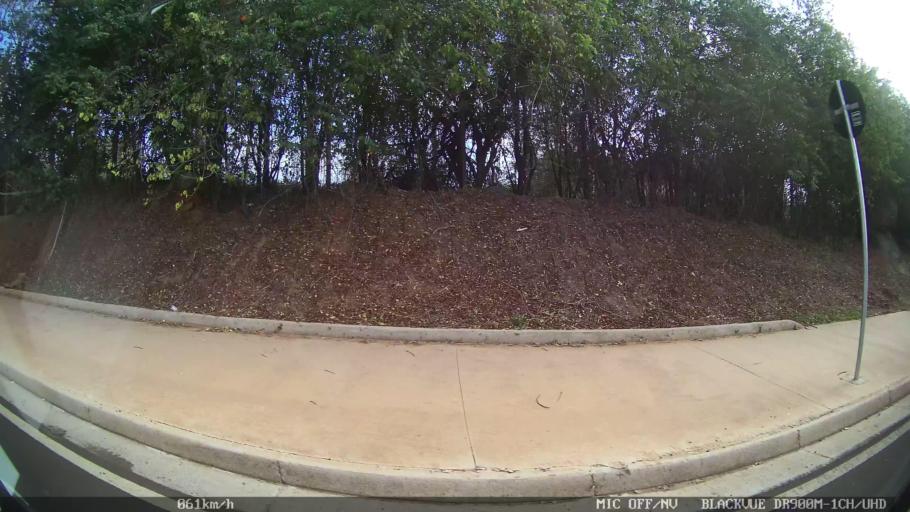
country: BR
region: Sao Paulo
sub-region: Sao Jose Do Rio Preto
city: Sao Jose do Rio Preto
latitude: -20.8097
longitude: -49.4313
